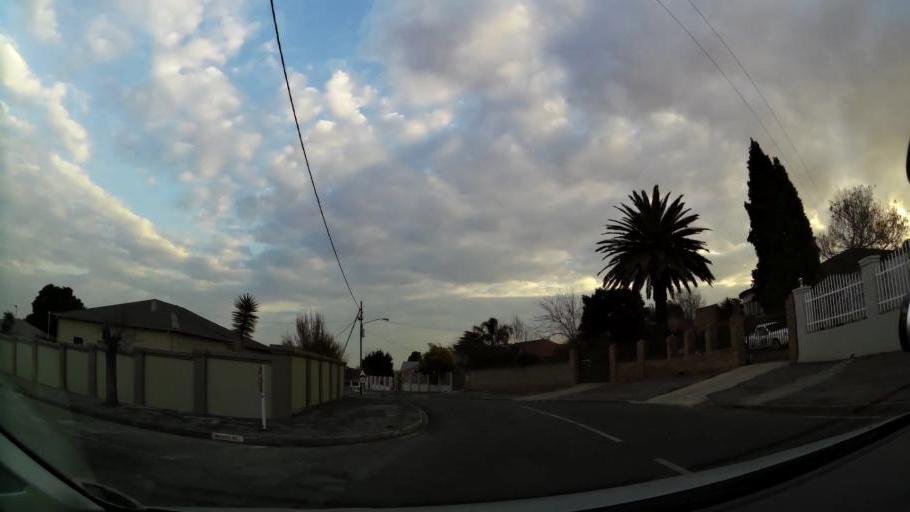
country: ZA
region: Gauteng
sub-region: Ekurhuleni Metropolitan Municipality
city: Germiston
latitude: -26.1900
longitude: 28.1511
